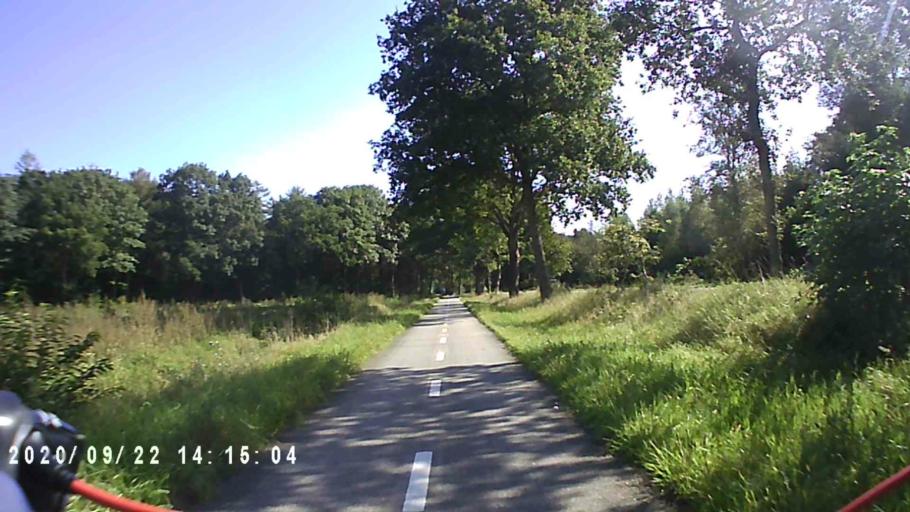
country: NL
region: Groningen
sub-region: Gemeente Leek
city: Leek
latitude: 53.0711
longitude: 6.4253
